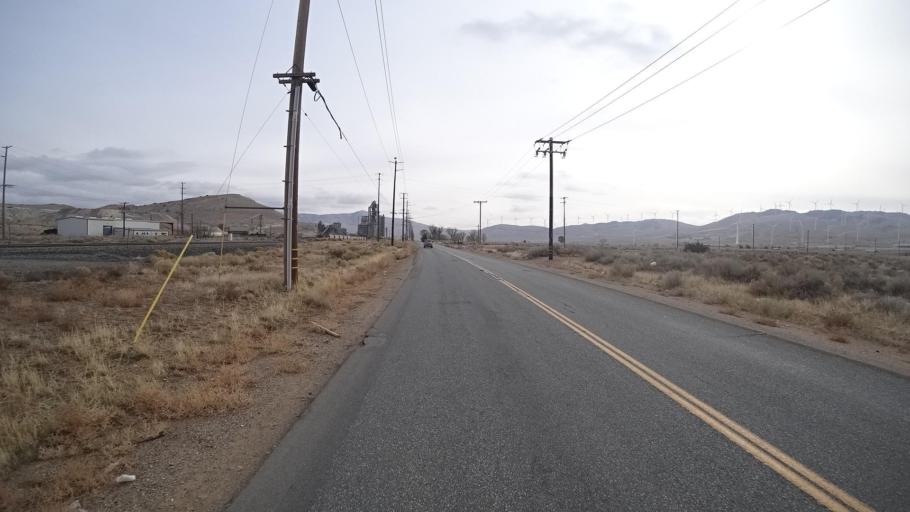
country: US
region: California
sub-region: Kern County
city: Tehachapi
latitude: 35.1226
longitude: -118.3783
